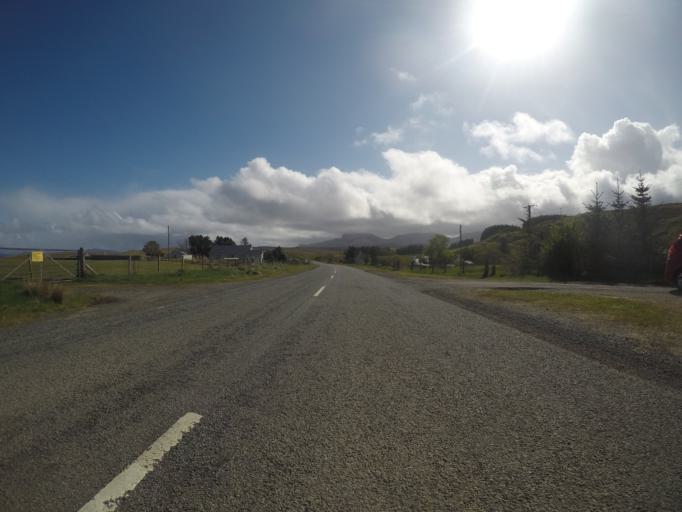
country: GB
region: Scotland
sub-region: Highland
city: Portree
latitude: 57.5848
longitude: -6.1577
